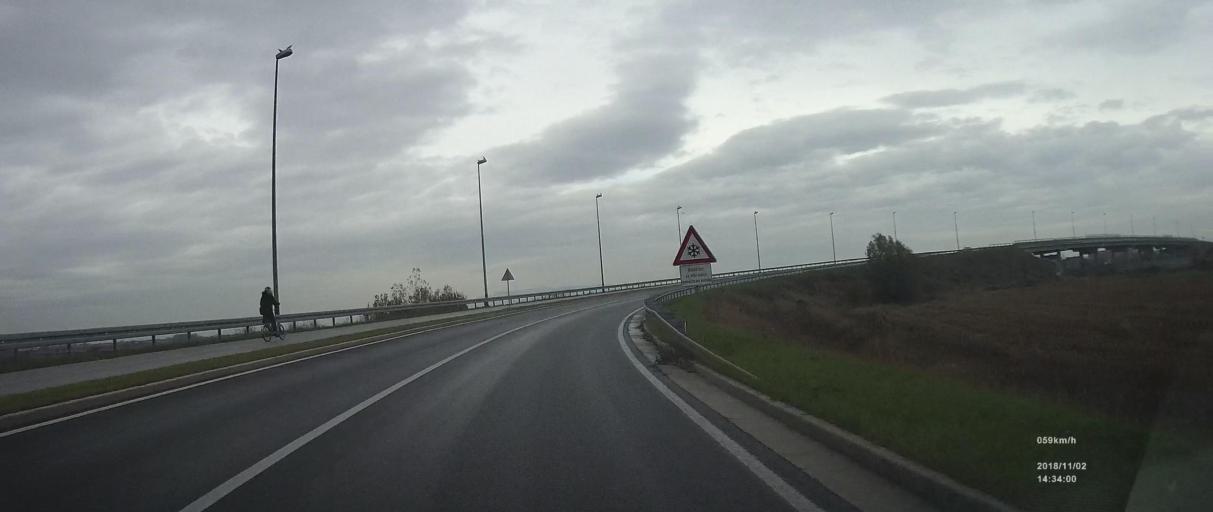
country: HR
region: Zagrebacka
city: Gradici
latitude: 45.6957
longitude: 16.0591
